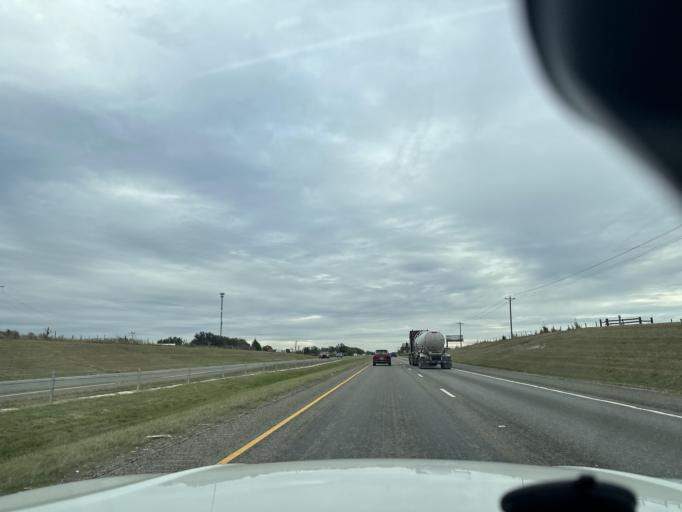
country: US
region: Texas
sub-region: Burleson County
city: Somerville
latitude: 30.1856
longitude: -96.5748
